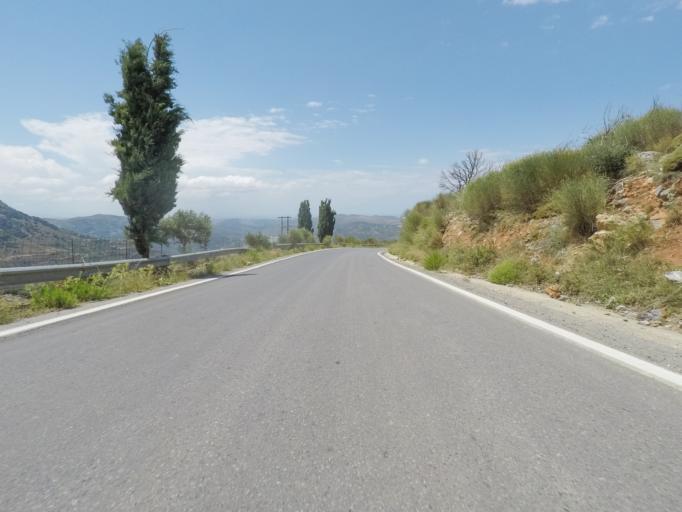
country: GR
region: Crete
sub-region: Nomos Irakleiou
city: Mokhos
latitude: 35.2147
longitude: 25.4594
